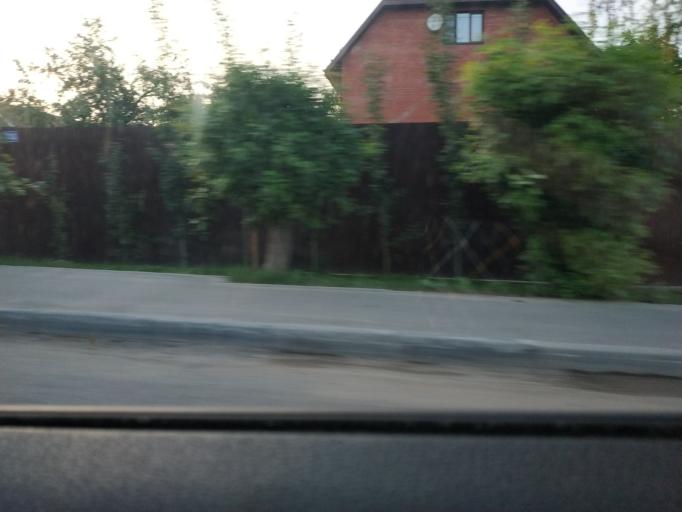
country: RU
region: Moskovskaya
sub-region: Shchelkovskiy Rayon
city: Grebnevo
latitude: 55.9740
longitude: 38.1054
